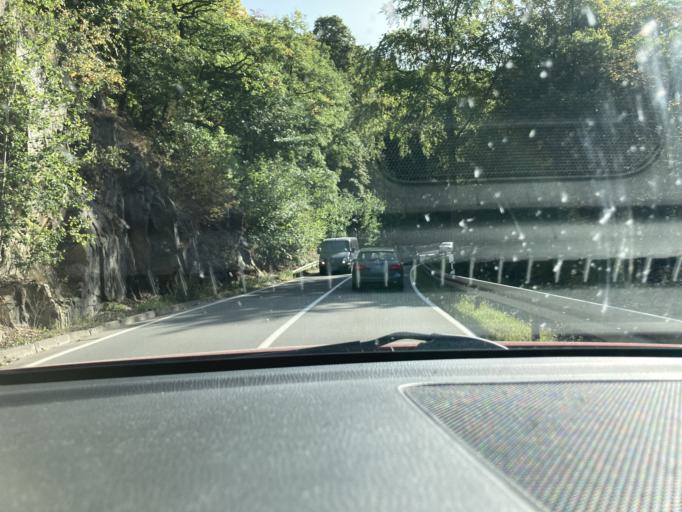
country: DE
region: Saxony-Anhalt
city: Thale
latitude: 51.7346
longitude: 11.0343
